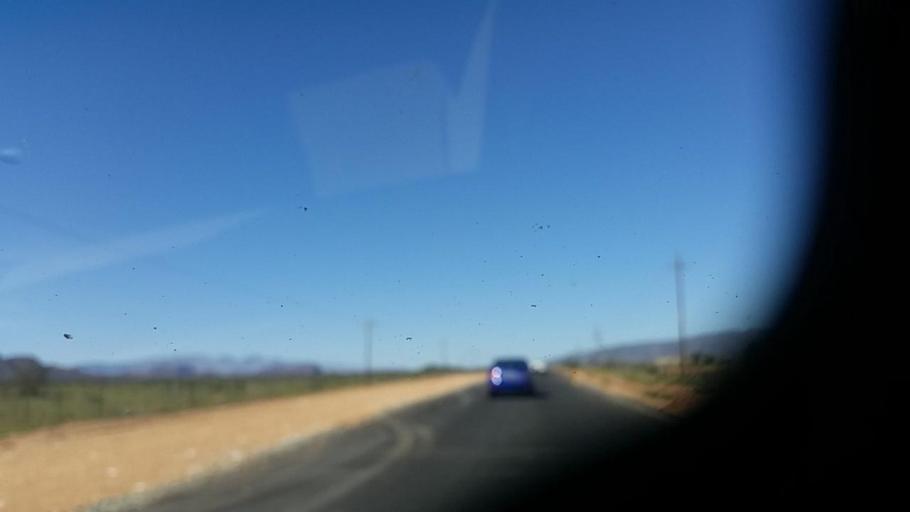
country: ZA
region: Western Cape
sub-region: Eden District Municipality
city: Oudtshoorn
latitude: -33.5765
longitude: 22.3283
